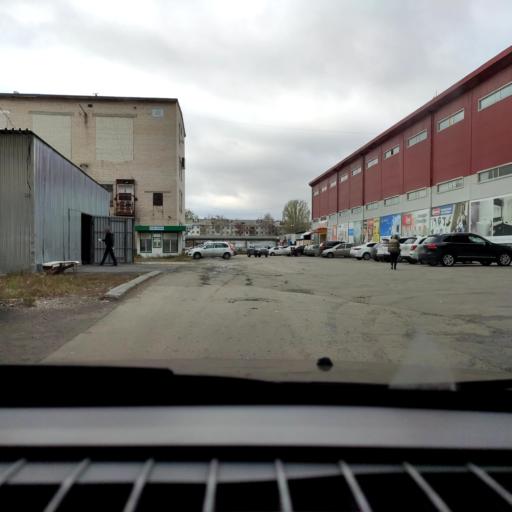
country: RU
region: Samara
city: Tol'yatti
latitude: 53.5080
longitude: 49.4065
